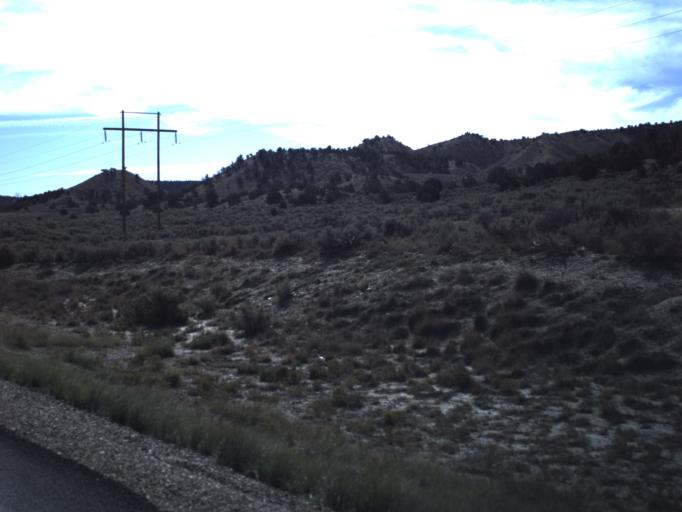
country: US
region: Utah
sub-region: Garfield County
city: Panguitch
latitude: 37.6015
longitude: -111.9591
